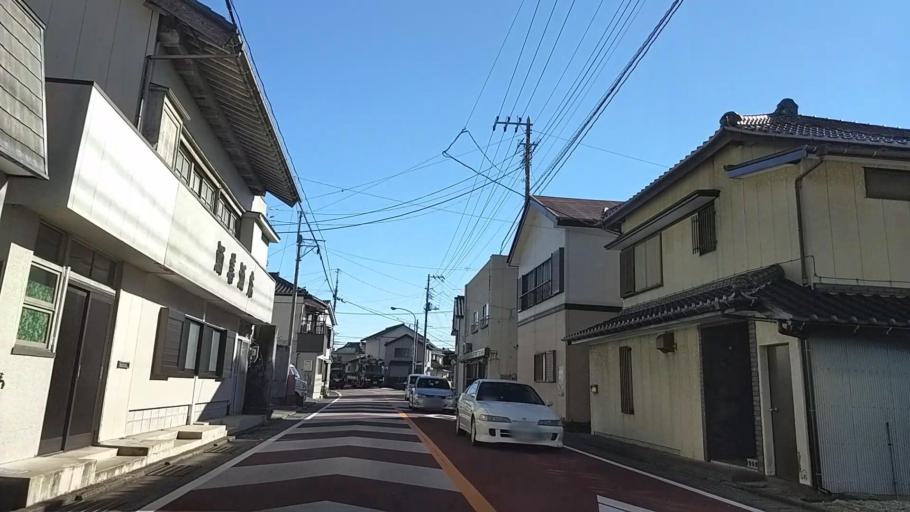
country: JP
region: Chiba
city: Kawaguchi
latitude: 35.0368
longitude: 140.0145
